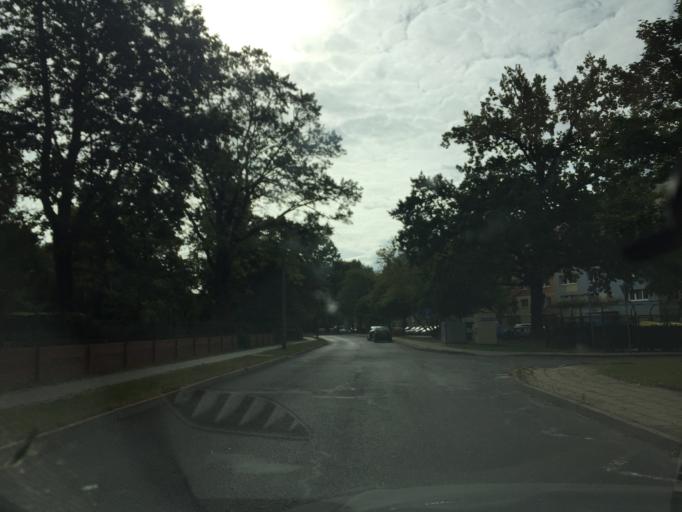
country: DE
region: Brandenburg
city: Erkner
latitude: 52.4173
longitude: 13.7594
